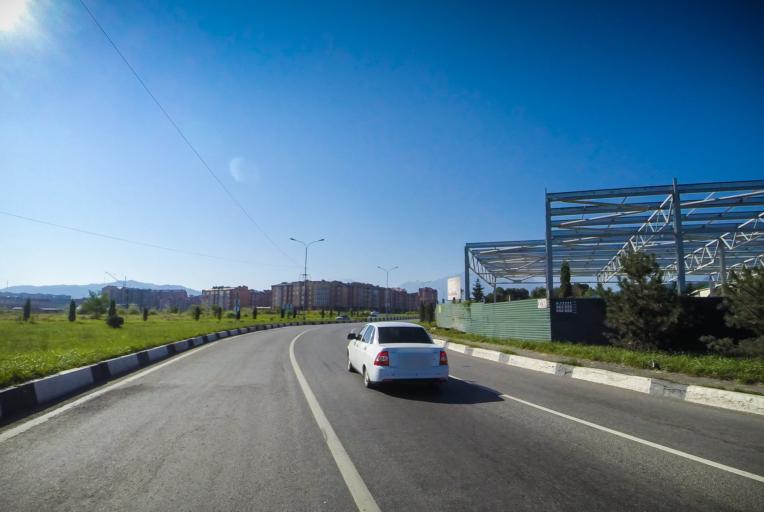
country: RU
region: North Ossetia
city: Vladikavkaz
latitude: 43.0249
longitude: 44.6442
